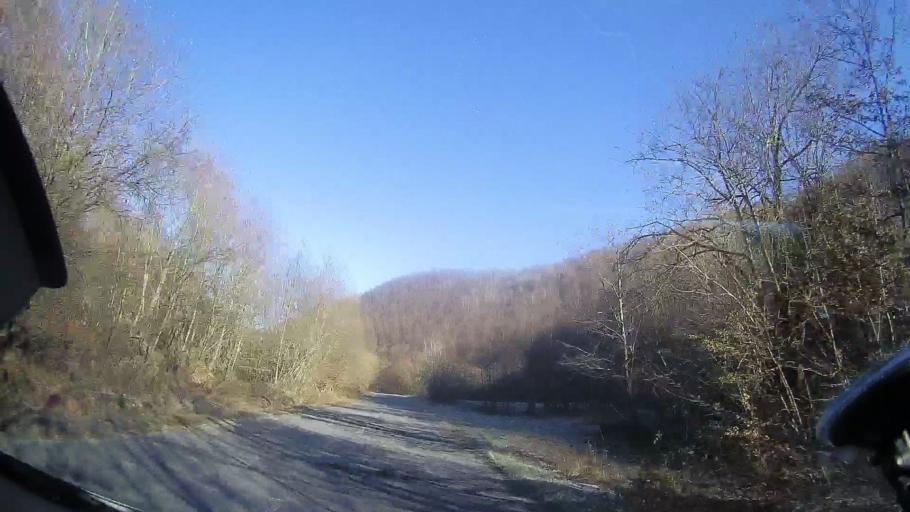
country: RO
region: Cluj
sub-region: Comuna Sacueu
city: Sacuieu
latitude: 46.8460
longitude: 22.8615
